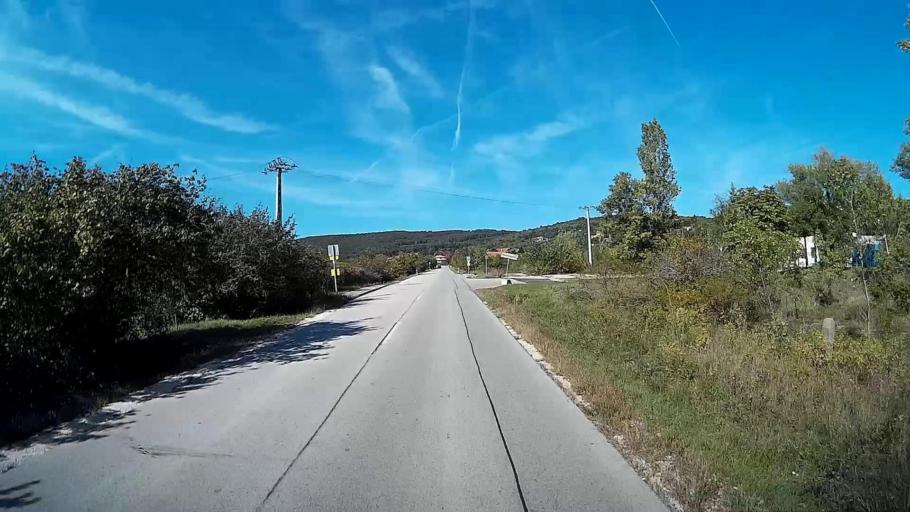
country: HU
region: Pest
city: Nagykovacsi
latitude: 47.6955
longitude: 19.0331
